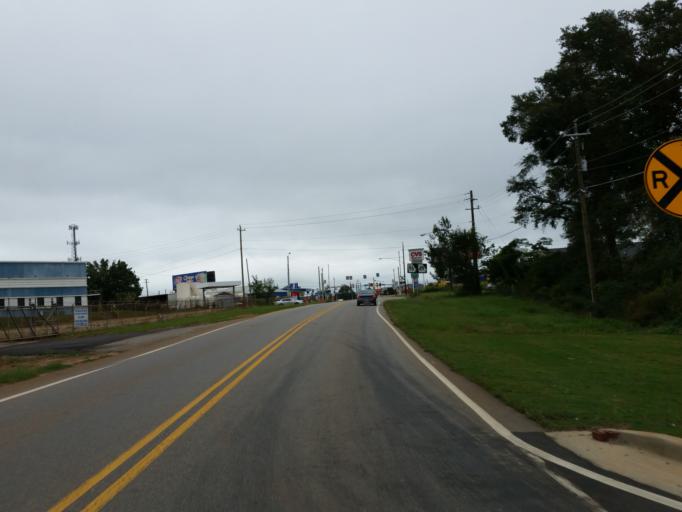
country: US
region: Georgia
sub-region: Peach County
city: Fort Valley
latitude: 32.5611
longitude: -83.8840
